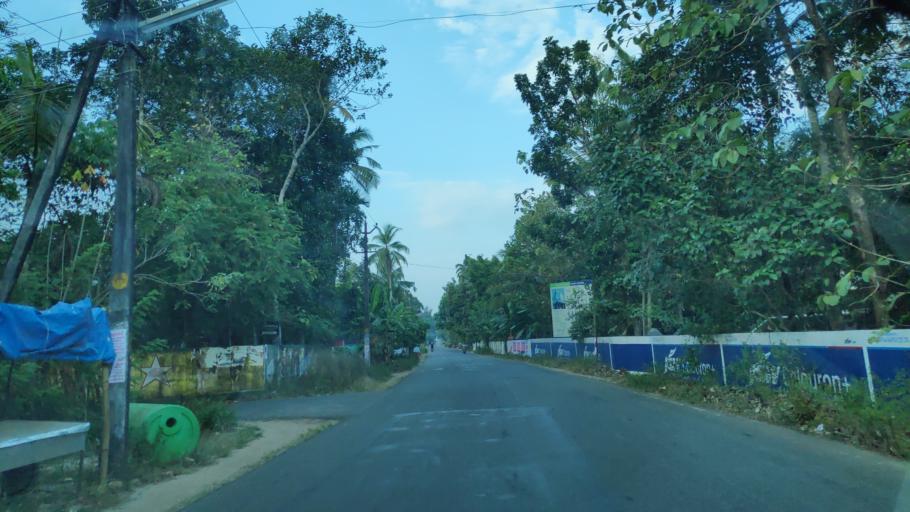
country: IN
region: Kerala
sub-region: Alappuzha
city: Shertallai
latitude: 9.6290
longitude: 76.3694
